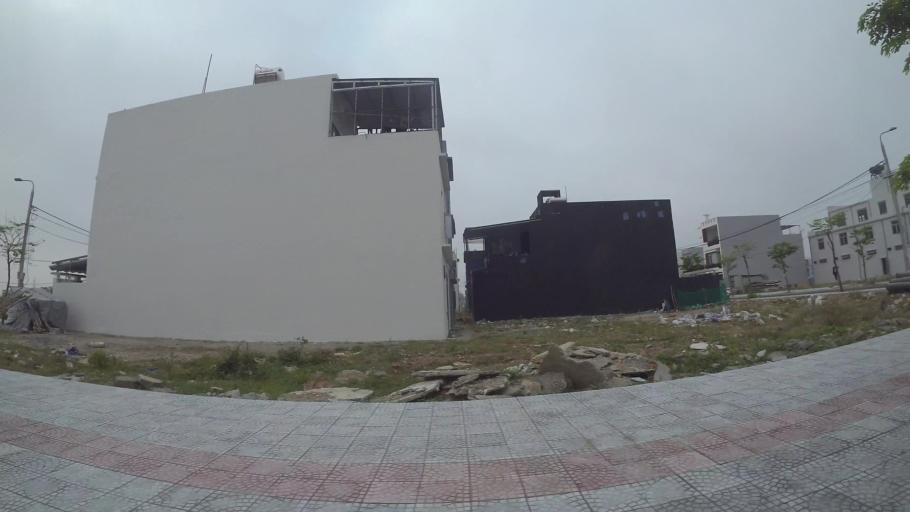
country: VN
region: Da Nang
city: Ngu Hanh Son
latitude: 16.0164
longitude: 108.2302
